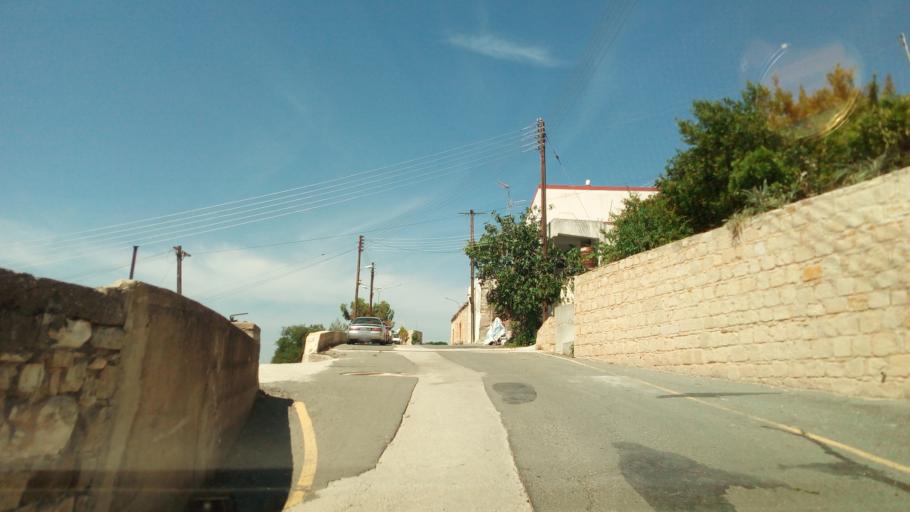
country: CY
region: Limassol
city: Pachna
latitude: 34.8008
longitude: 32.6799
